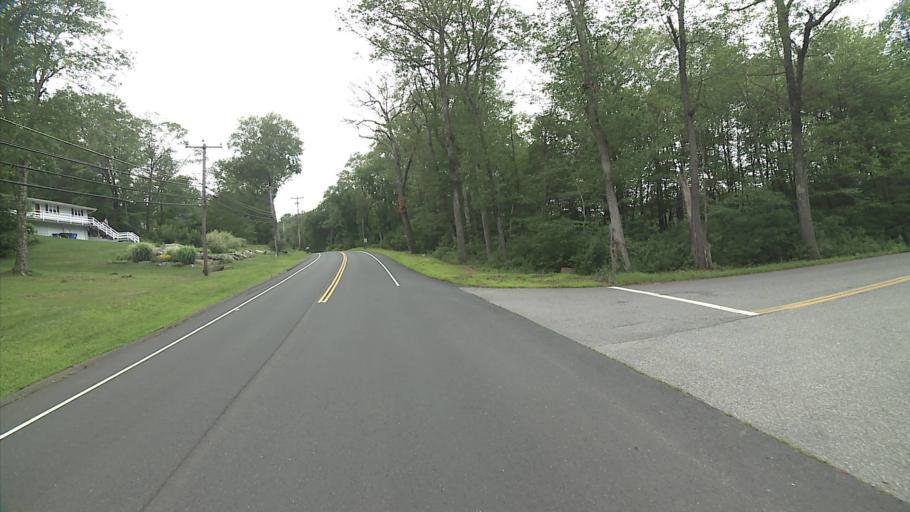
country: US
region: Connecticut
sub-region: Tolland County
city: Tolland
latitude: 41.8776
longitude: -72.3889
